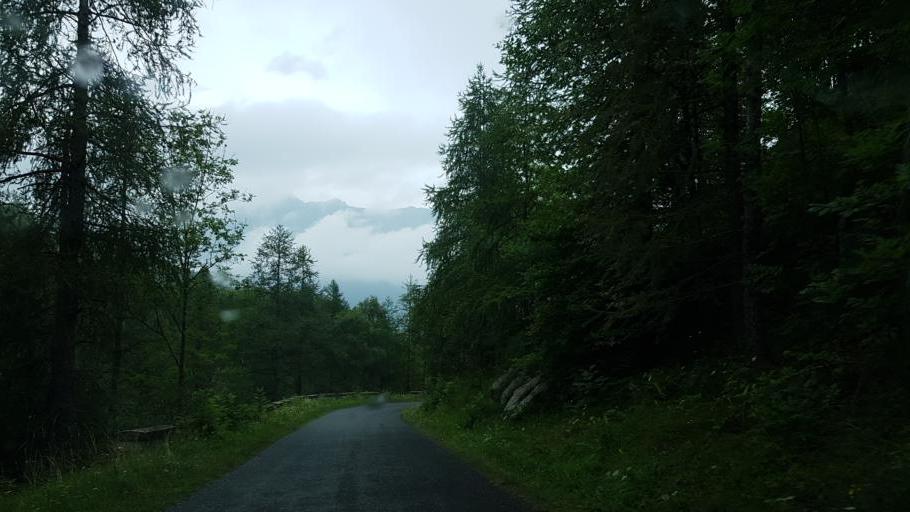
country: IT
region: Piedmont
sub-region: Provincia di Cuneo
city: Sampeyre
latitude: 44.5652
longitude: 7.1749
